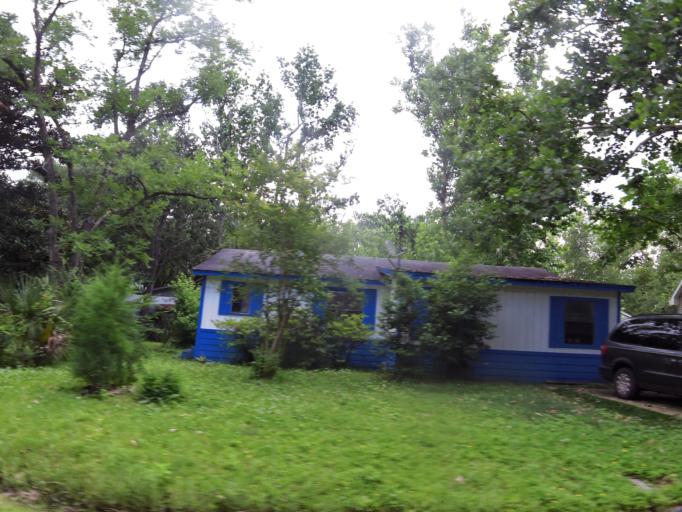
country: US
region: Florida
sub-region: Duval County
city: Jacksonville
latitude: 30.2859
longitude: -81.6456
